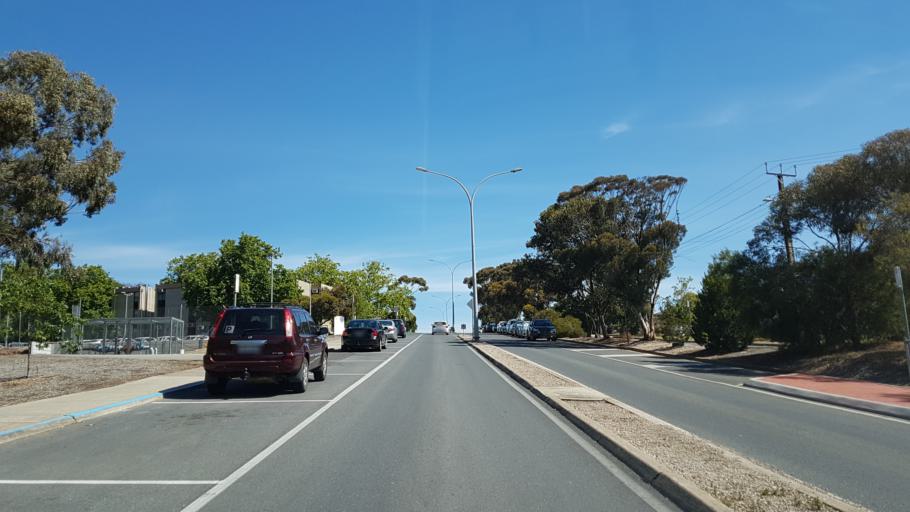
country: AU
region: South Australia
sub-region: Marion
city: Marion
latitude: -35.0242
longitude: 138.5679
